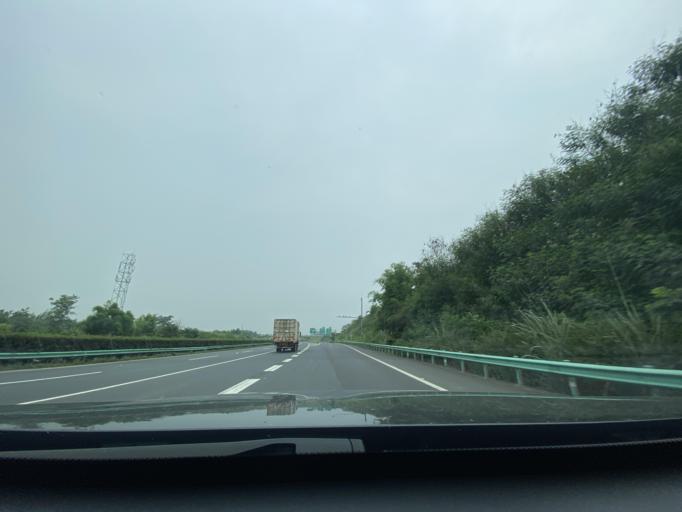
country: CN
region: Sichuan
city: Longquan
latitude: 30.3377
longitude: 104.1189
